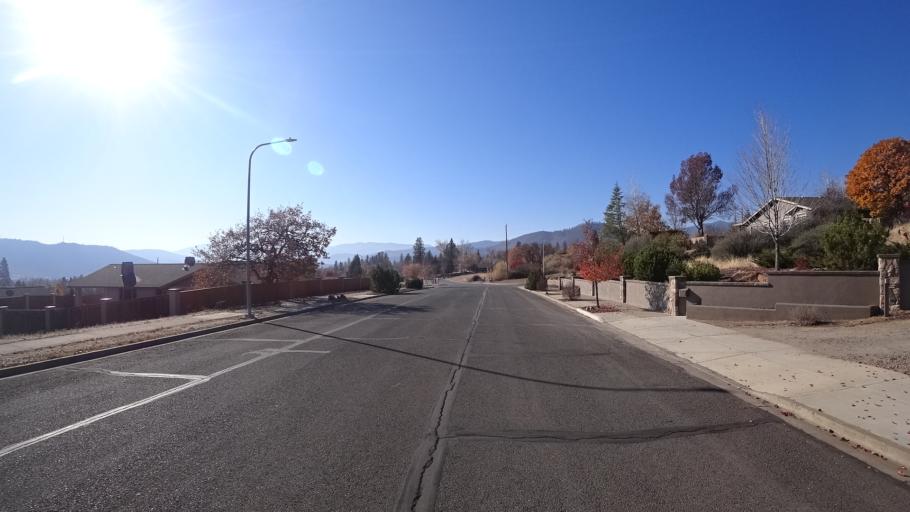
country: US
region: California
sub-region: Siskiyou County
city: Yreka
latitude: 41.7436
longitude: -122.6441
